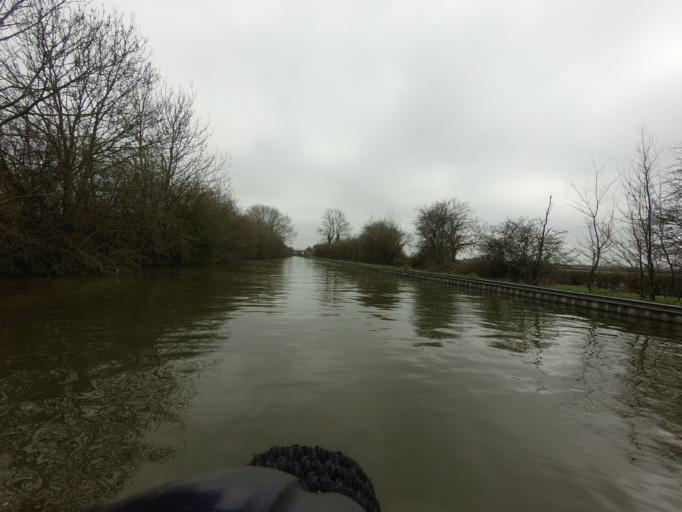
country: GB
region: England
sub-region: Buckinghamshire
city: Cheddington
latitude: 51.8806
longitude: -0.6595
